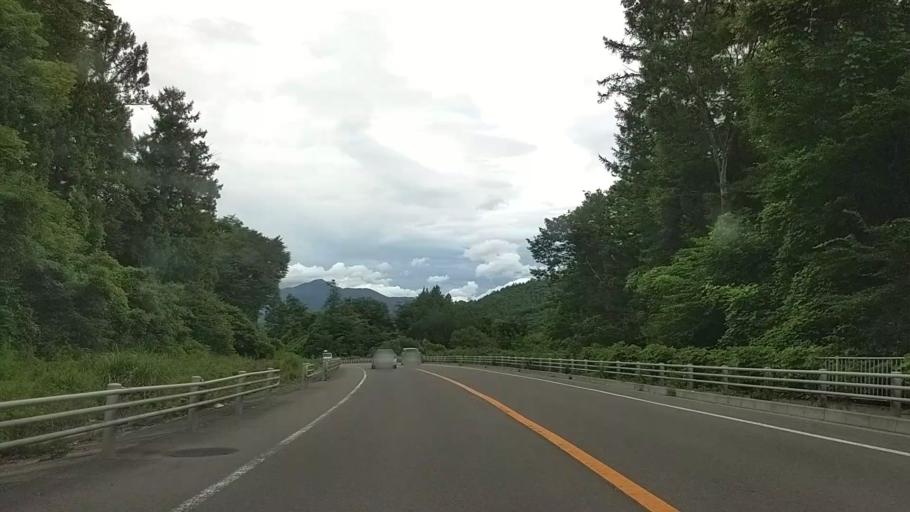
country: JP
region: Yamanashi
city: Otsuki
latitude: 35.5582
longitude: 138.9376
